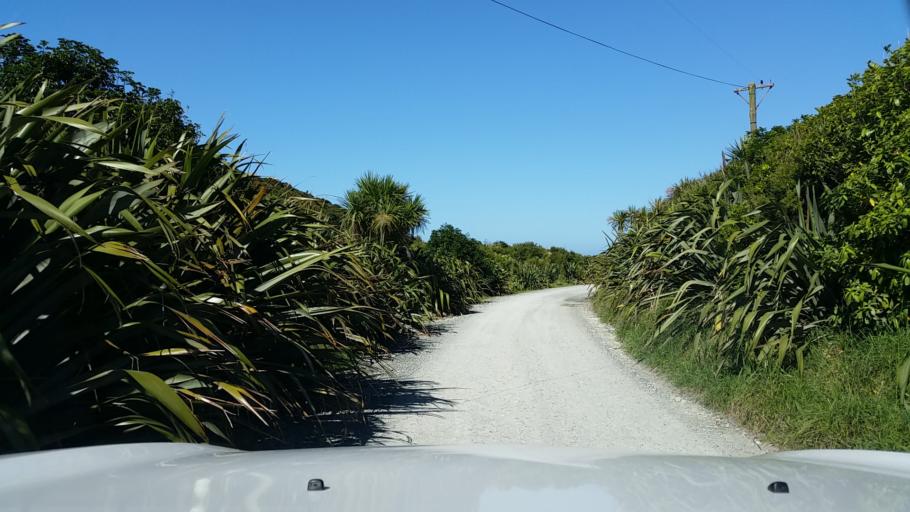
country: NZ
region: Auckland
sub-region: Auckland
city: Titirangi
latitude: -37.0378
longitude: 174.5101
